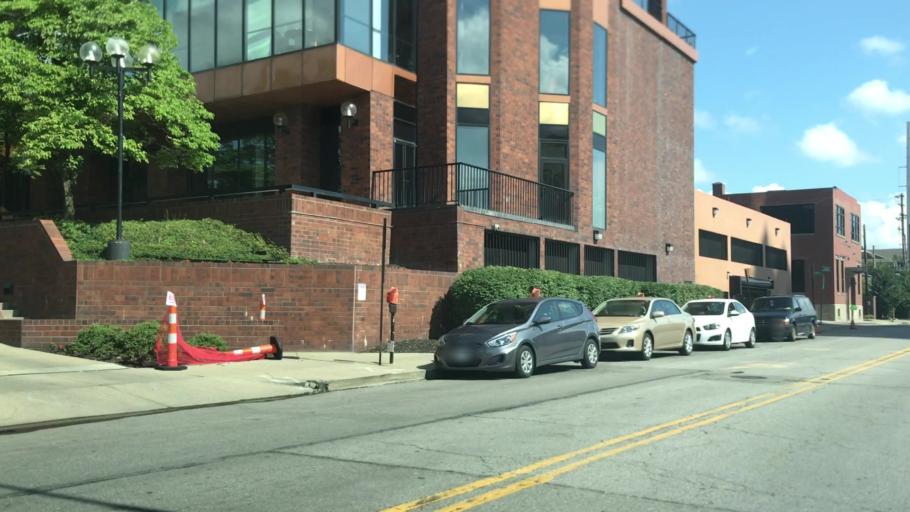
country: US
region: Ohio
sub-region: Franklin County
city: Columbus
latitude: 39.9554
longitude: -83.0043
